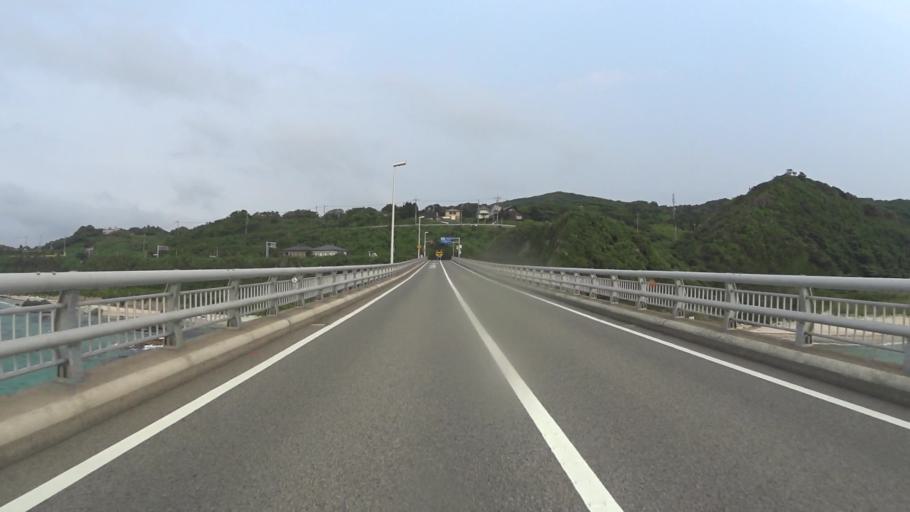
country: JP
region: Yamaguchi
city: Nagato
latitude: 34.3486
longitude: 130.8938
